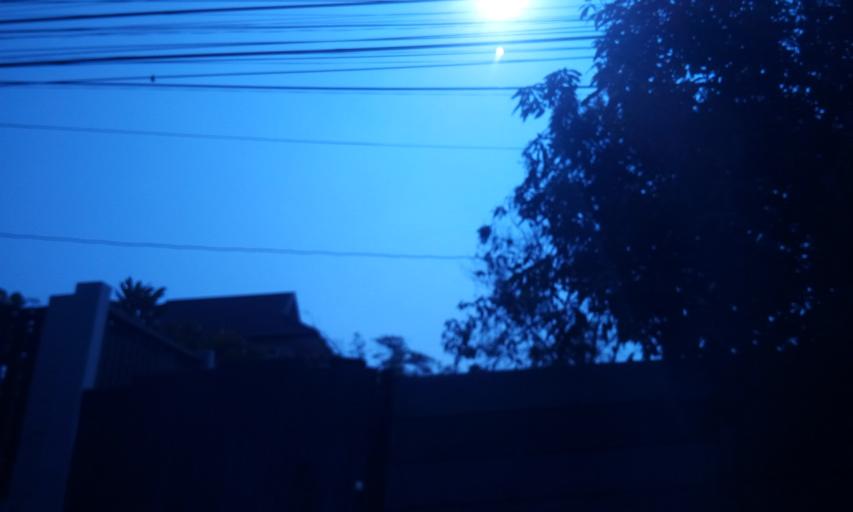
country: TH
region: Pathum Thani
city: Lam Luk Ka
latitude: 13.9600
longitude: 100.7058
